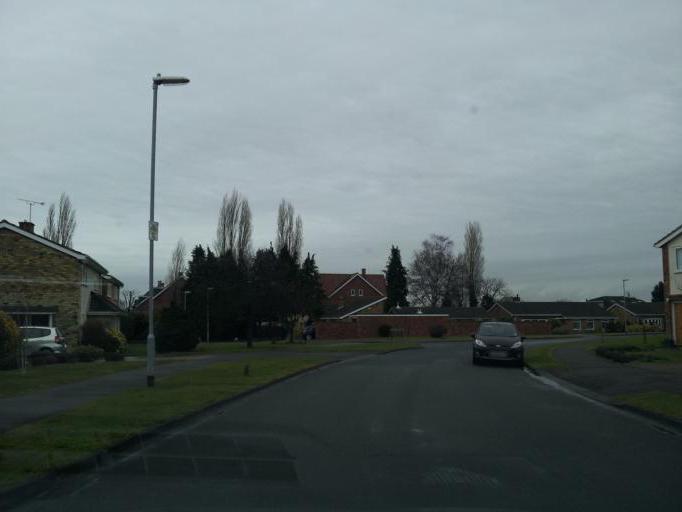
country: GB
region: England
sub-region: Cambridgeshire
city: Bottisham
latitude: 52.2235
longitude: 0.2617
